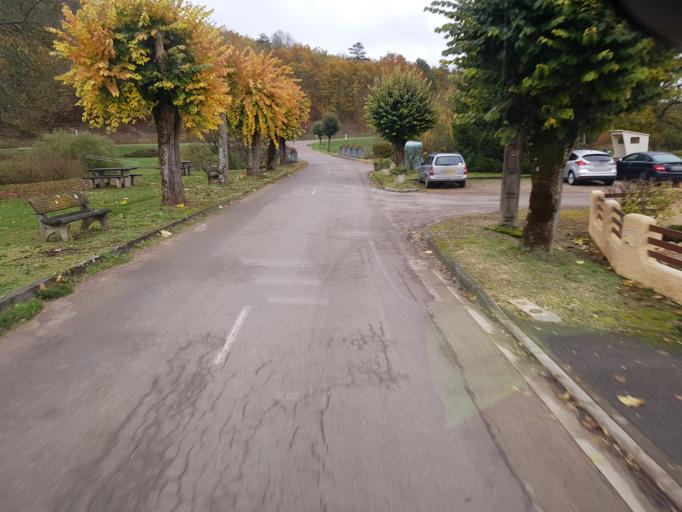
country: FR
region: Bourgogne
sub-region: Departement de la Cote-d'Or
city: Is-sur-Tille
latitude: 47.5329
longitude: 4.9868
